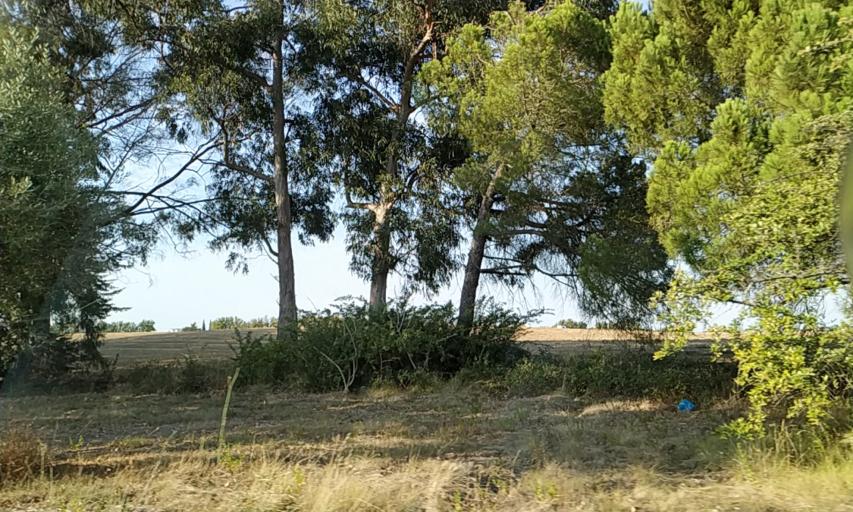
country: PT
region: Santarem
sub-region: Santarem
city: Santarem
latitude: 39.3113
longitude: -8.6673
